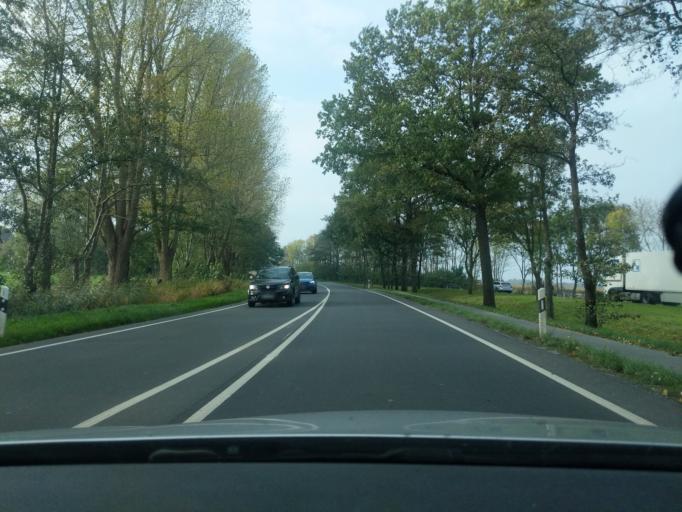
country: DE
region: Lower Saxony
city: Belum
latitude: 53.8077
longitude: 9.0152
